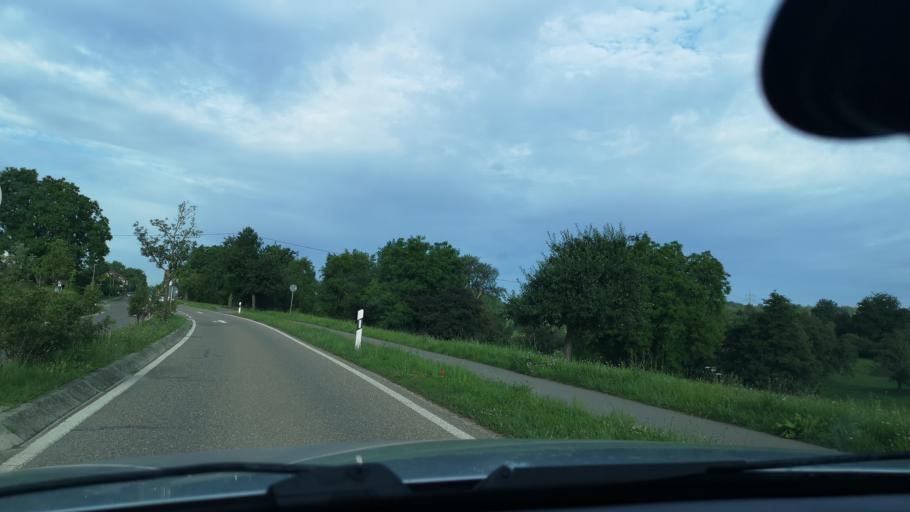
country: DE
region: Baden-Wuerttemberg
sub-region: Regierungsbezirk Stuttgart
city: Ohmden
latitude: 48.6490
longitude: 9.5347
